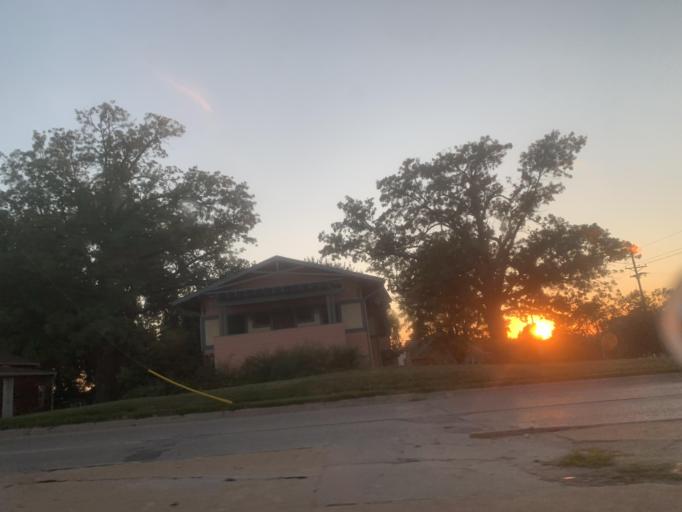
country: US
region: Nebraska
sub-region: Douglas County
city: Omaha
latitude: 41.2140
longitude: -95.9763
